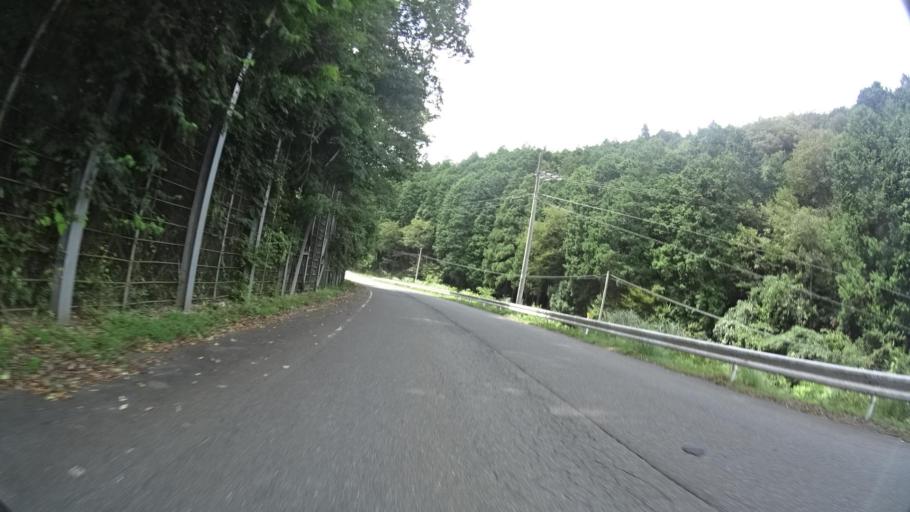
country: JP
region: Kyoto
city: Miyazu
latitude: 35.4428
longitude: 135.1581
